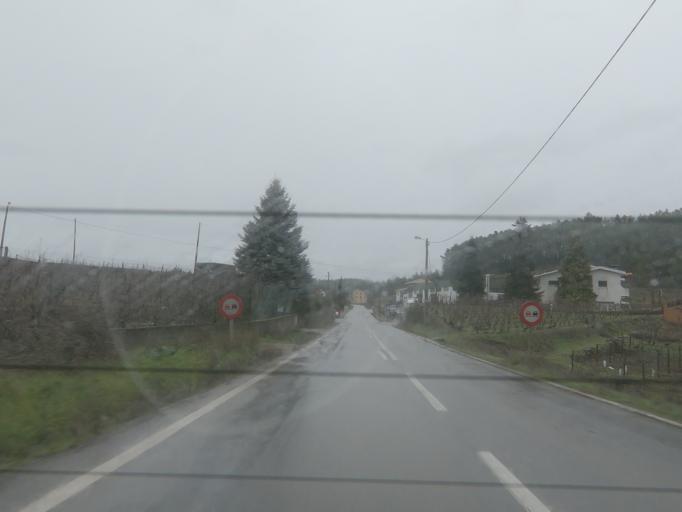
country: PT
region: Vila Real
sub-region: Sabrosa
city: Vilela
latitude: 41.2176
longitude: -7.6745
